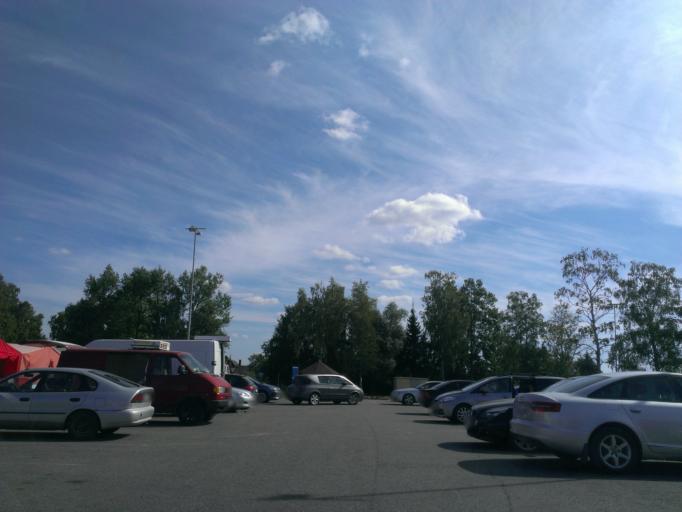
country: LV
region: Adazi
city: Adazi
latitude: 57.0708
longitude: 24.3202
